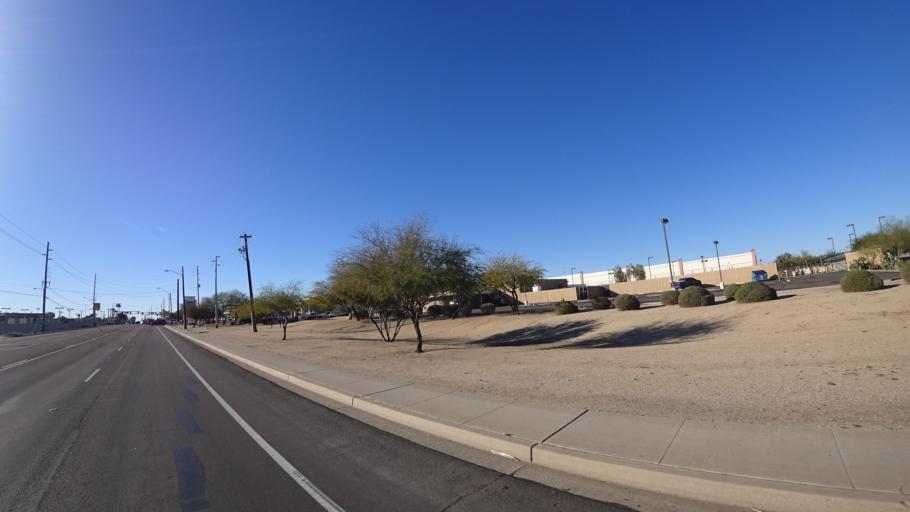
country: US
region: Arizona
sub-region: Maricopa County
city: Avondale
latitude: 33.4499
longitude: -112.3380
